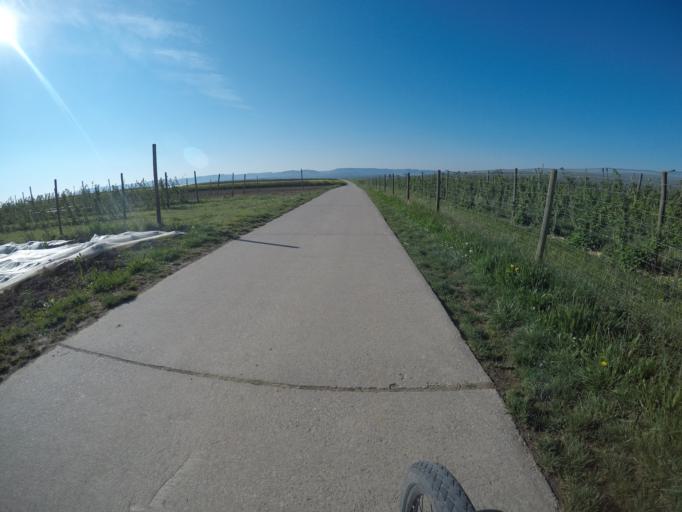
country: DE
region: Baden-Wuerttemberg
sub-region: Regierungsbezirk Stuttgart
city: Wolfschlugen
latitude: 48.6459
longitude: 9.2595
